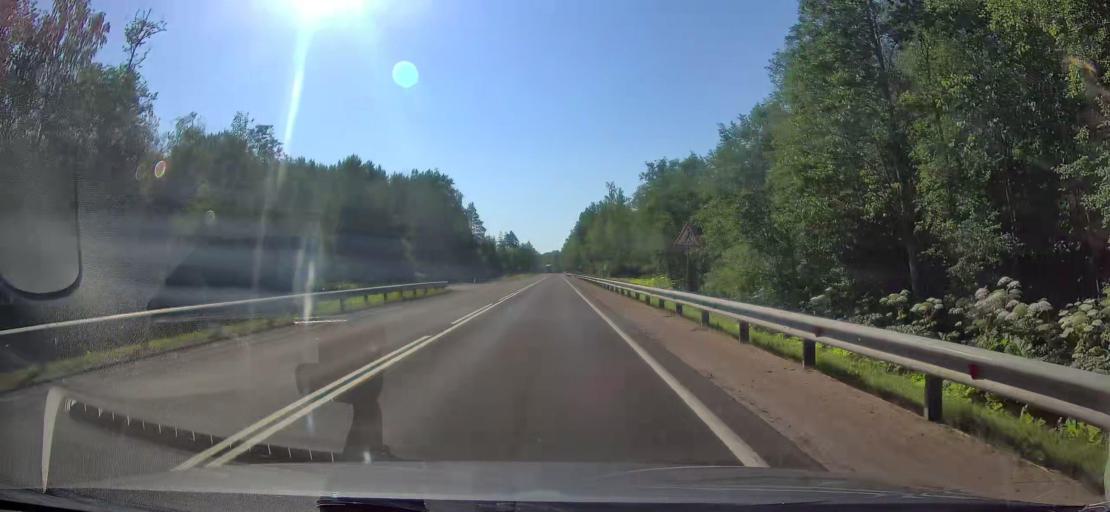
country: RU
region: Leningrad
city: Khvalovo
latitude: 59.8841
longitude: 32.8399
